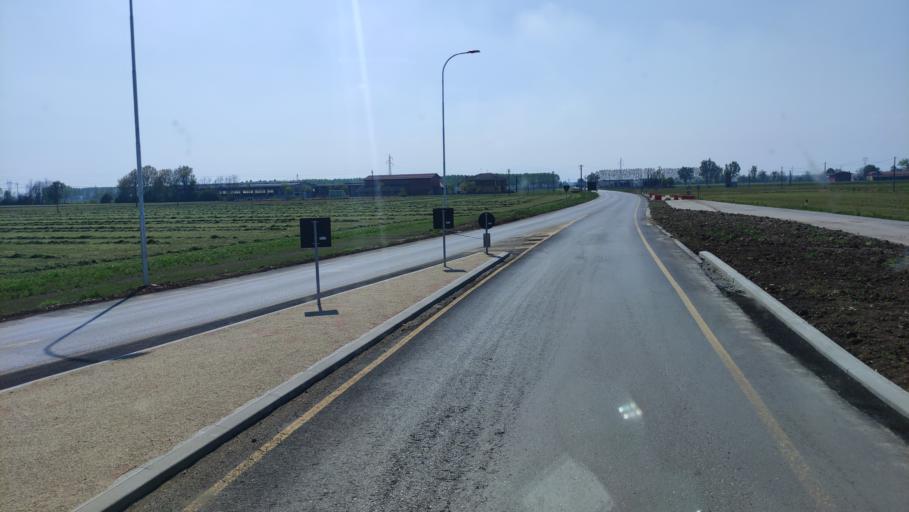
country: IT
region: Piedmont
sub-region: Provincia di Cuneo
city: Marene
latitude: 44.6566
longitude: 7.7155
